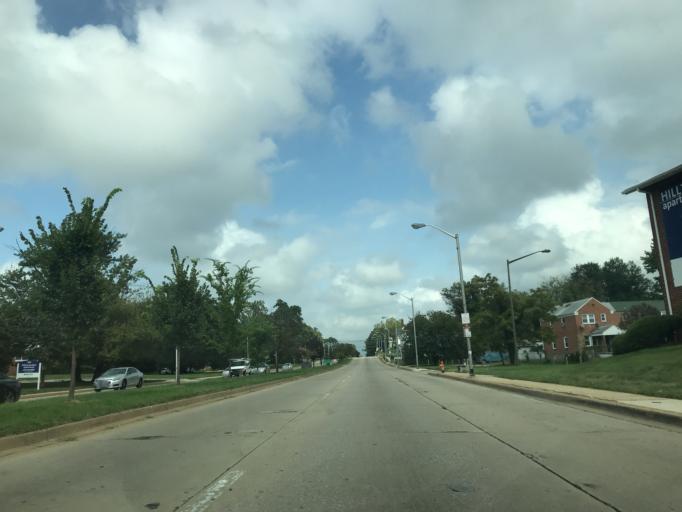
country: US
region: Maryland
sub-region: Baltimore County
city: Lochearn
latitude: 39.3495
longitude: -76.6901
